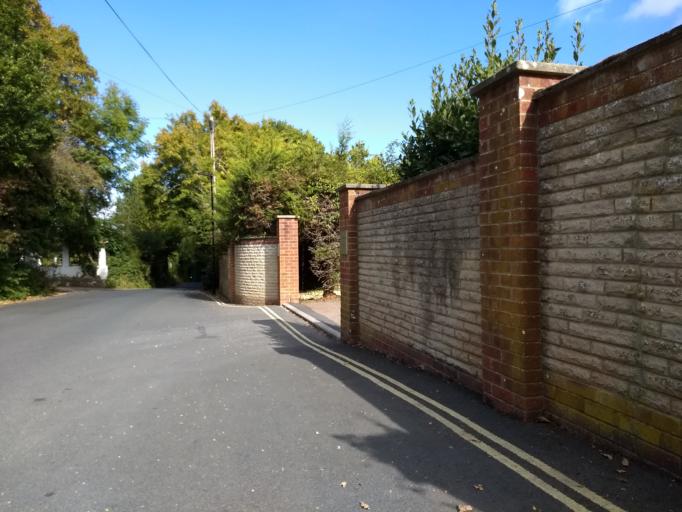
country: GB
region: England
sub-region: Isle of Wight
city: Seaview
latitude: 50.7211
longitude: -1.1244
